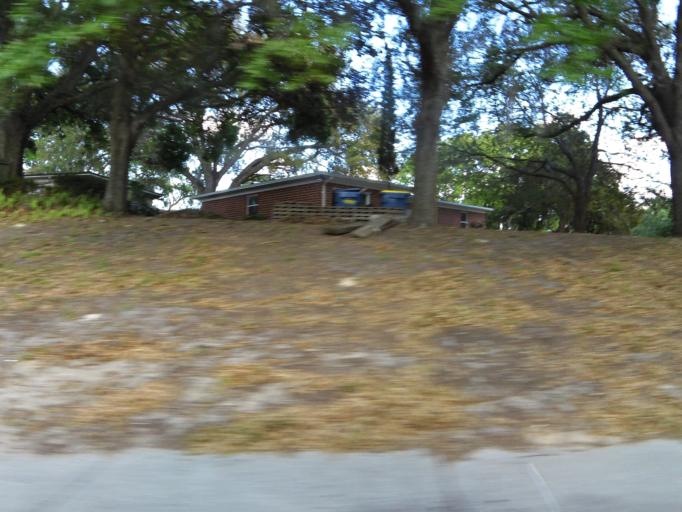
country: US
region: Florida
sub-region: Duval County
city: Jacksonville
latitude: 30.3433
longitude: -81.5973
